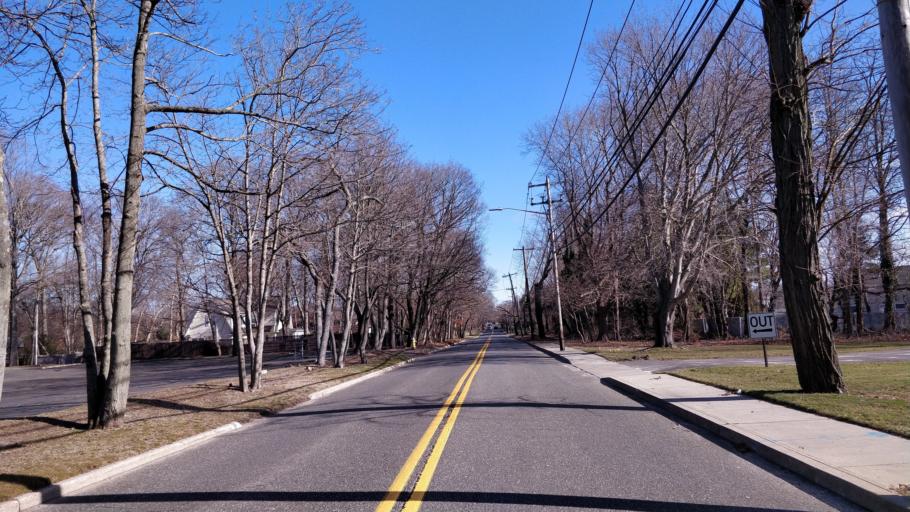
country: US
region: New York
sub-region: Suffolk County
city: Village of the Branch
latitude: 40.8666
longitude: -73.1869
